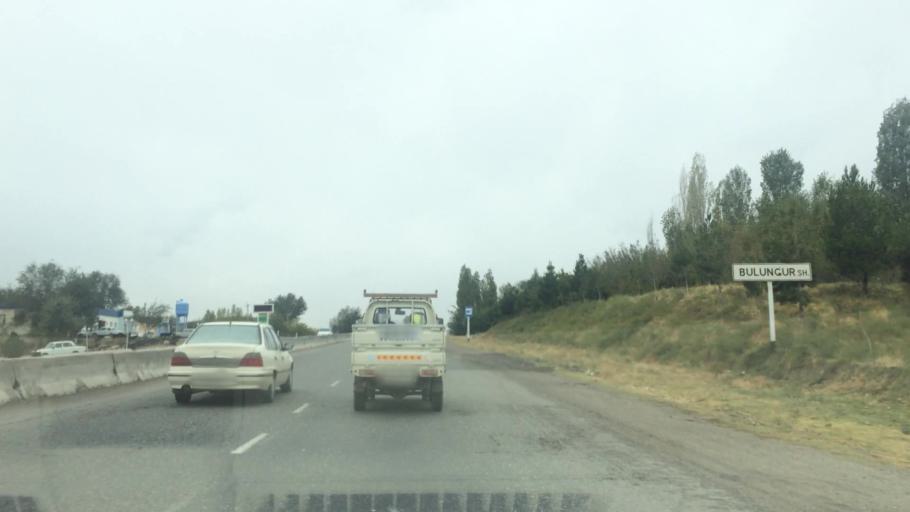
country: UZ
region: Samarqand
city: Bulung'ur
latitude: 39.7727
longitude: 67.2786
